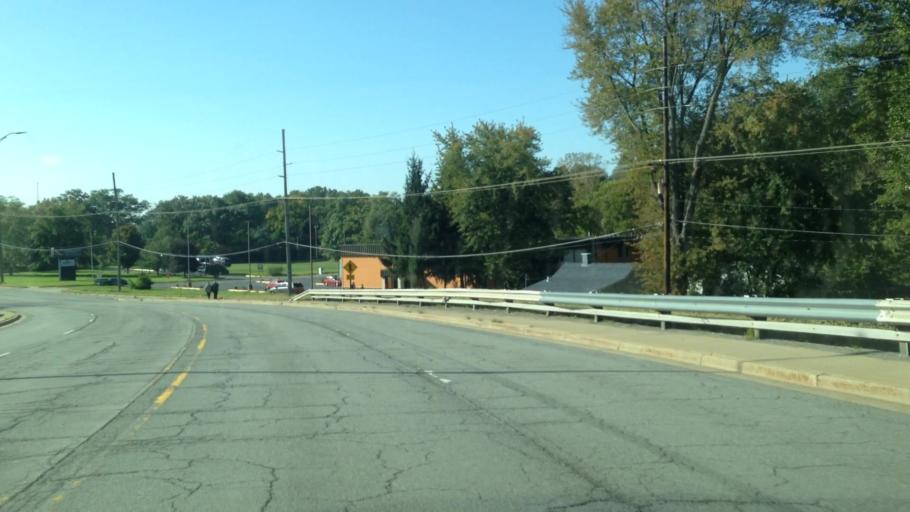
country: US
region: Indiana
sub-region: Porter County
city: Portage
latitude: 41.5863
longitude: -87.1829
